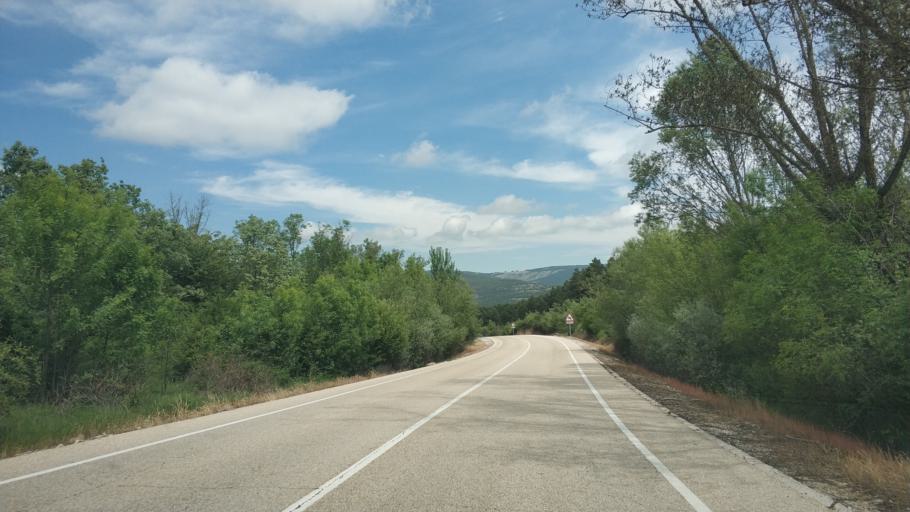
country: ES
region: Castille and Leon
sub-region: Provincia de Soria
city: Cidones
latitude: 41.8364
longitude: -2.5915
